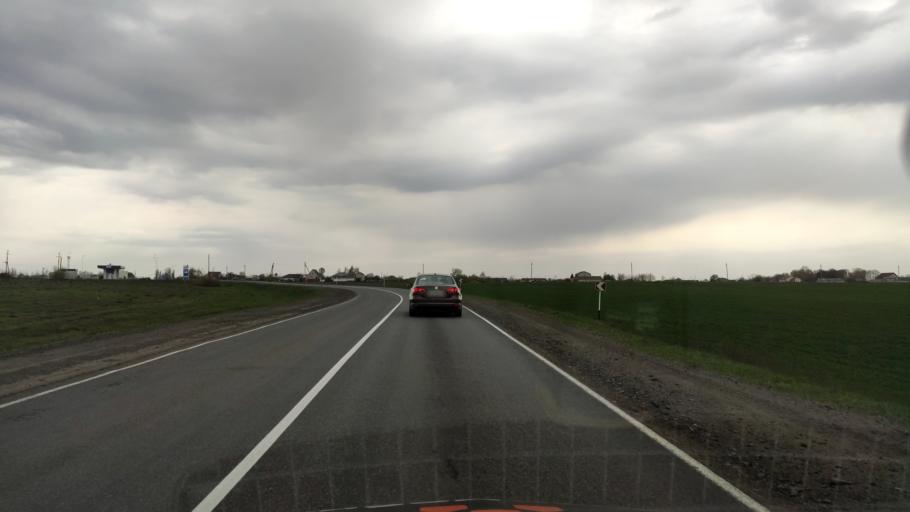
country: RU
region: Kursk
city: Gorshechnoye
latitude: 51.5378
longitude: 38.0222
